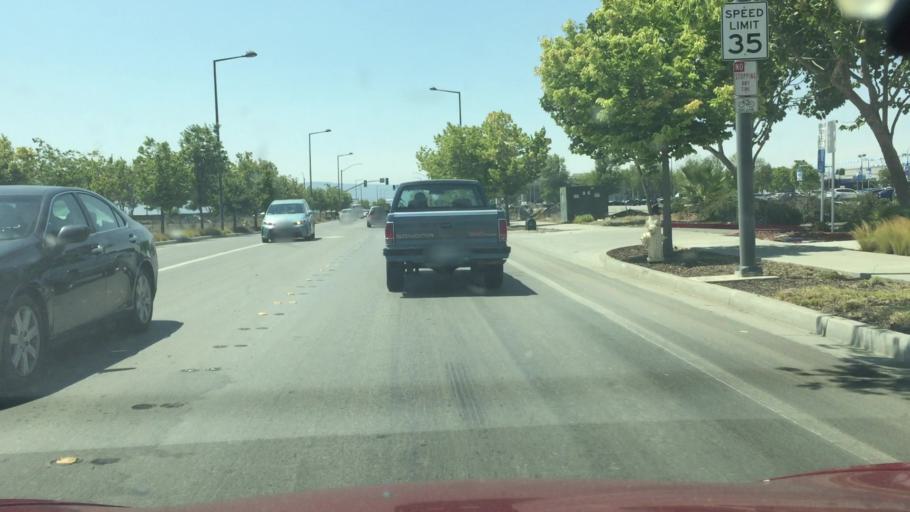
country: US
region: California
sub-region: Alameda County
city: Fremont
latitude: 37.4985
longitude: -121.9709
